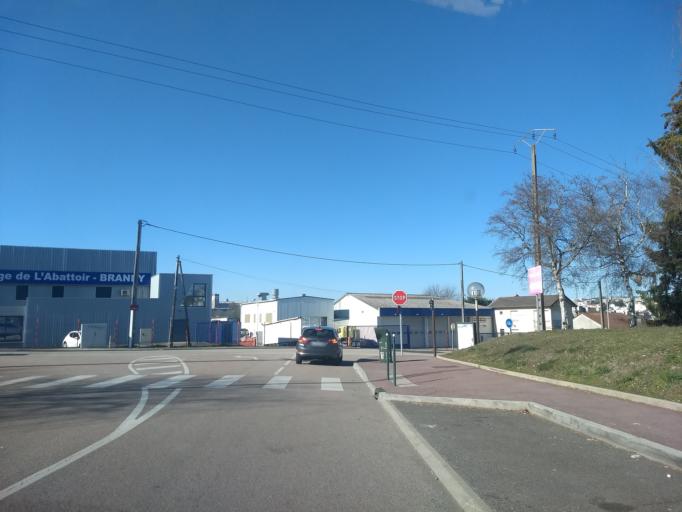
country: FR
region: Limousin
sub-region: Departement de la Haute-Vienne
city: Limoges
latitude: 45.8118
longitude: 1.2582
